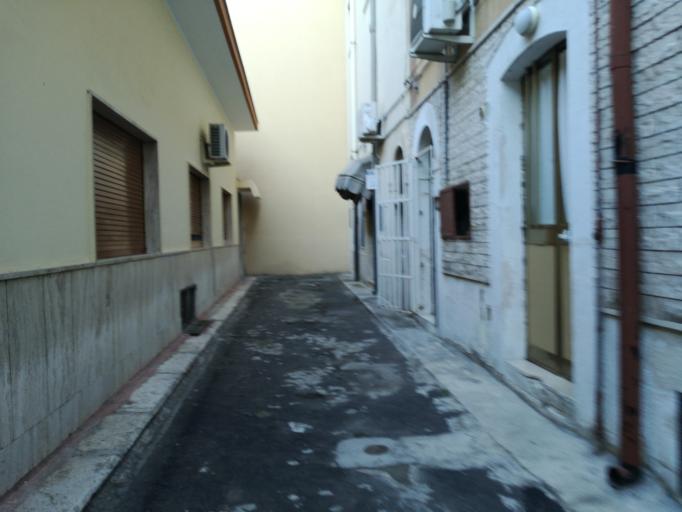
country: IT
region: Apulia
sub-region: Provincia di Bari
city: Triggiano
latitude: 41.0652
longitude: 16.9278
